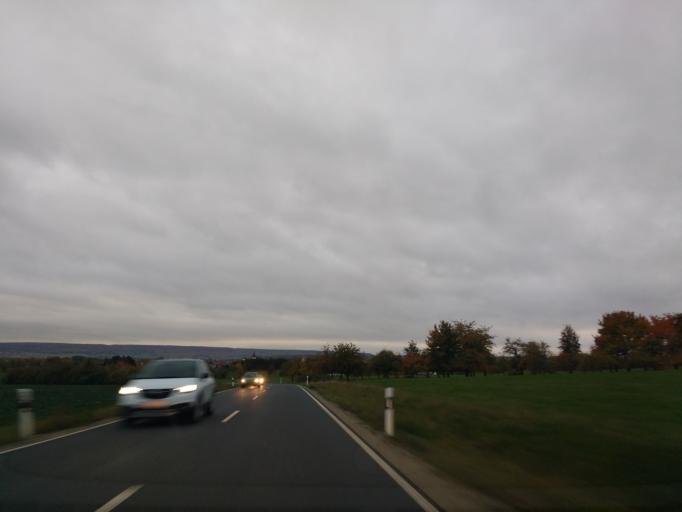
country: DE
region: Thuringia
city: Buhla
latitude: 51.4244
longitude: 10.4349
